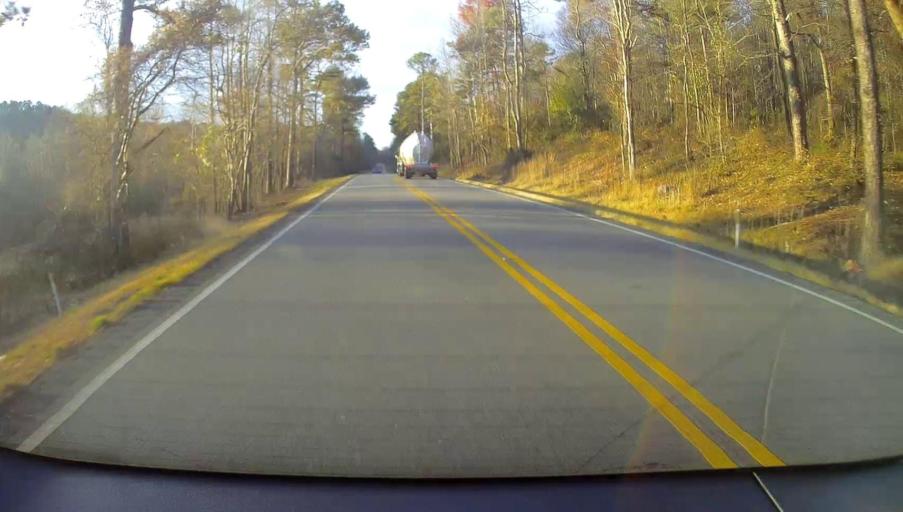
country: US
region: Alabama
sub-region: Blount County
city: Oneonta
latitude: 34.0759
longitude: -86.3336
